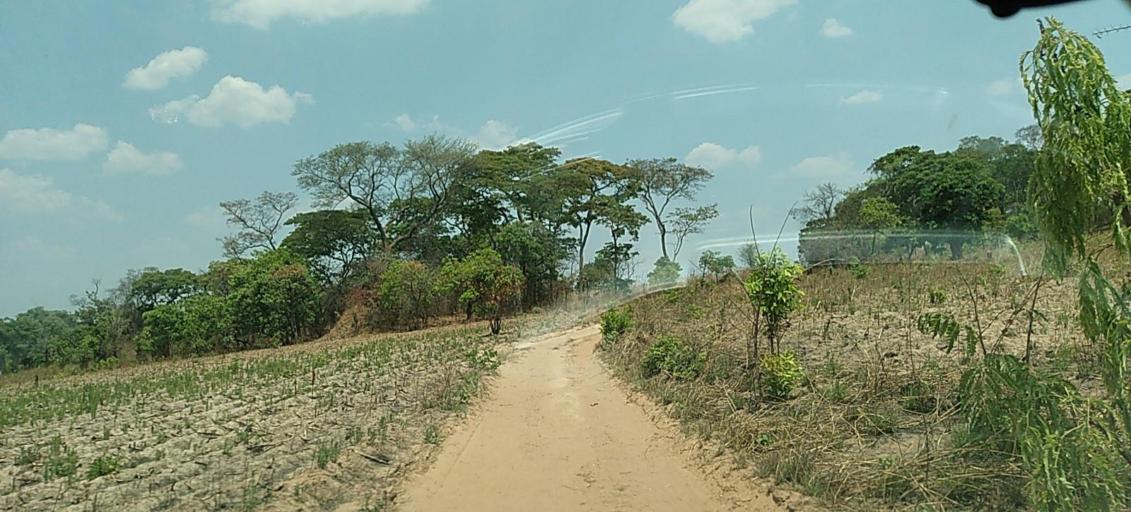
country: ZM
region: North-Western
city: Kasempa
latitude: -13.5296
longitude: 25.8229
